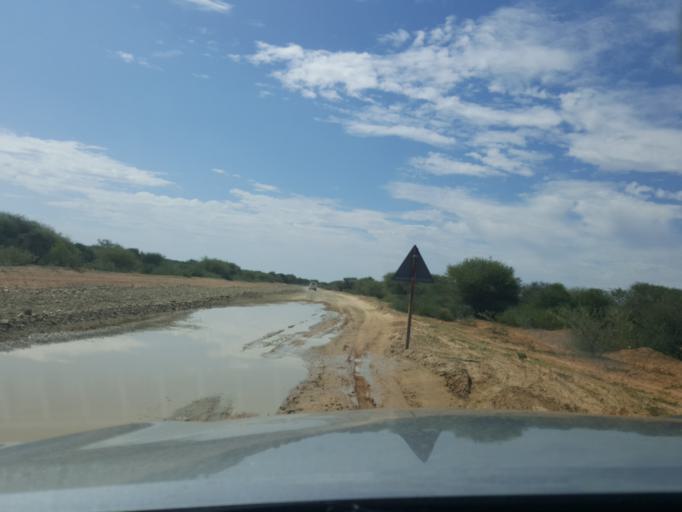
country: BW
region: Kweneng
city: Letlhakeng
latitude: -23.9831
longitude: 24.9676
